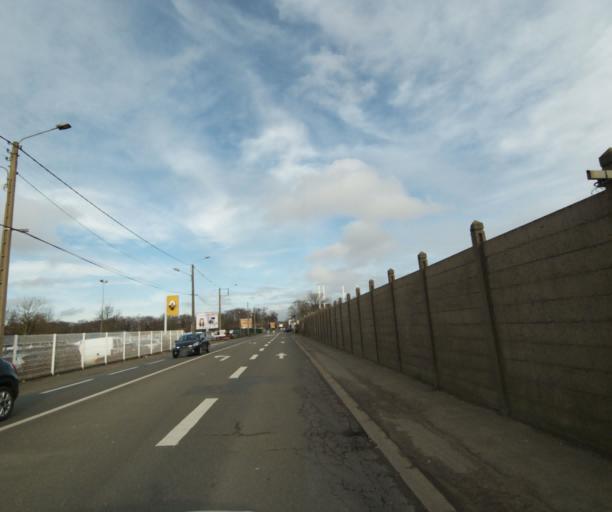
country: FR
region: Pays de la Loire
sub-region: Departement de la Sarthe
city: Allonnes
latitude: 47.9780
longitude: 0.1771
